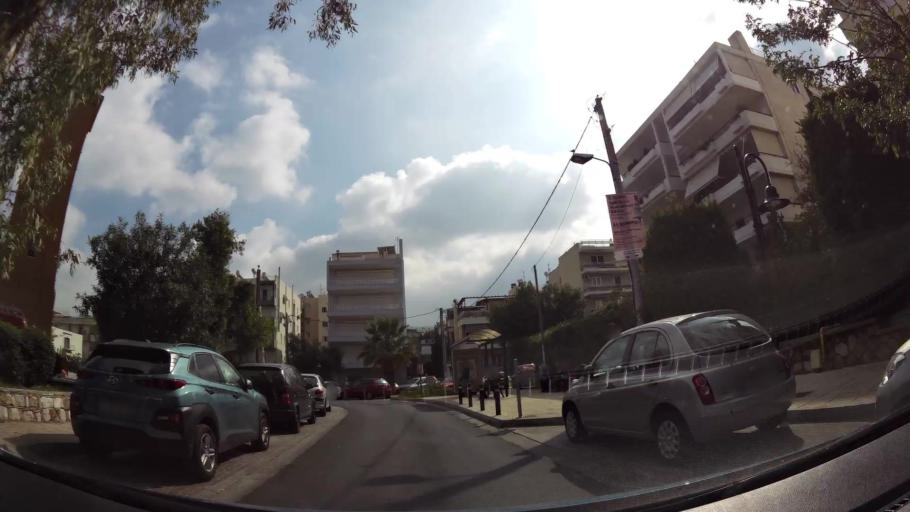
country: GR
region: Attica
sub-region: Nomarchia Athinas
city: Cholargos
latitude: 38.0036
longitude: 23.7966
